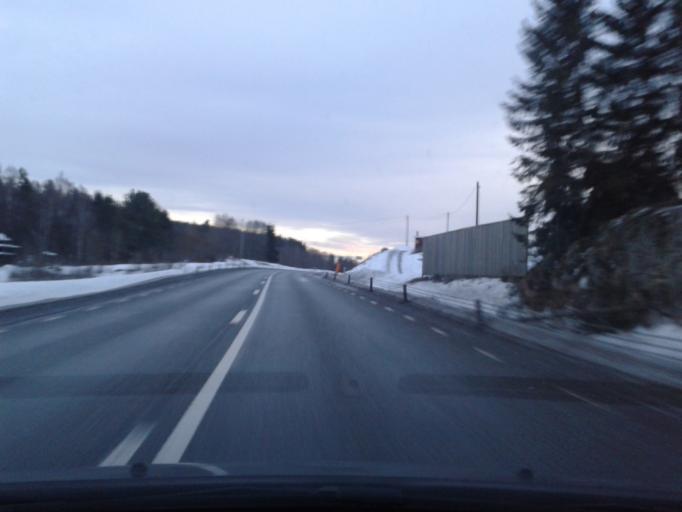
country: SE
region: Vaesternorrland
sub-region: Kramfors Kommun
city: Bollstabruk
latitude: 63.0300
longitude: 17.6720
